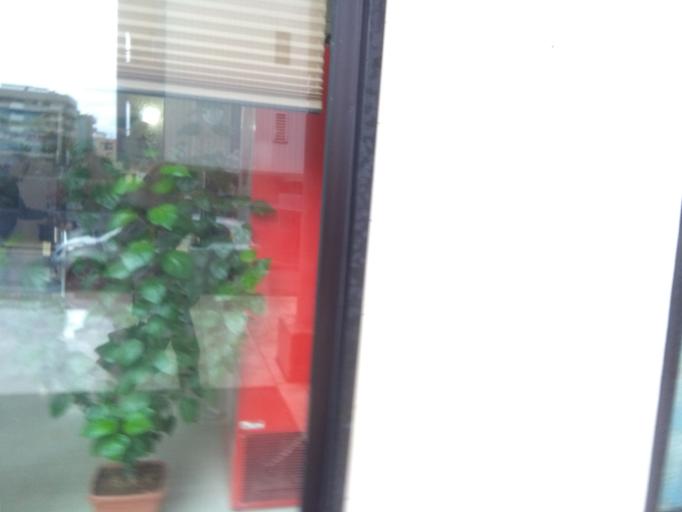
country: IT
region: Apulia
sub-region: Provincia di Bari
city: San Paolo
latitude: 41.1381
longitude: 16.8184
